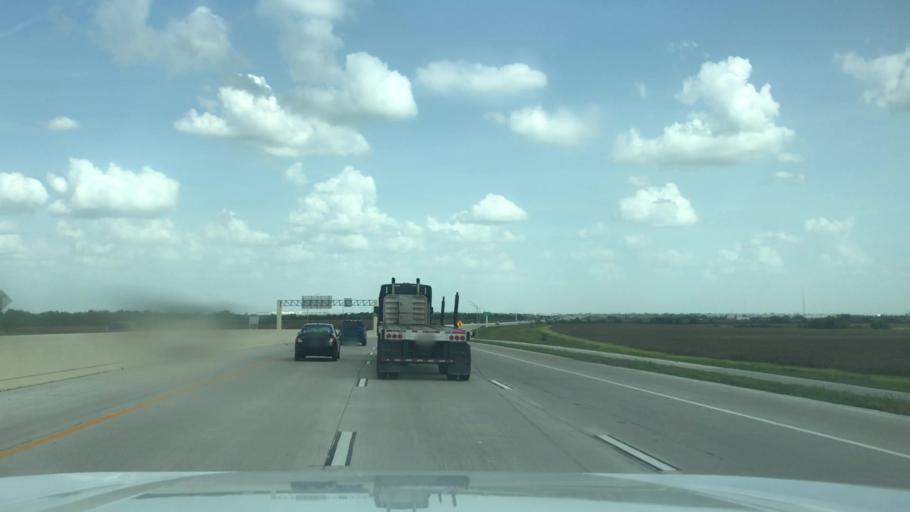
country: US
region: Texas
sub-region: Waller County
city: Waller
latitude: 30.0572
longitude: -95.8902
